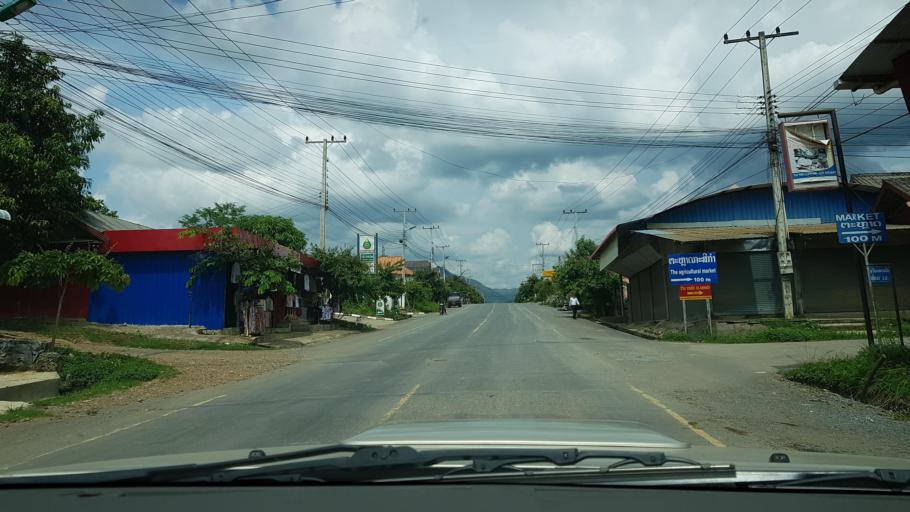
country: LA
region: Loungnamtha
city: Muang Nale
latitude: 20.1474
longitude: 101.4631
